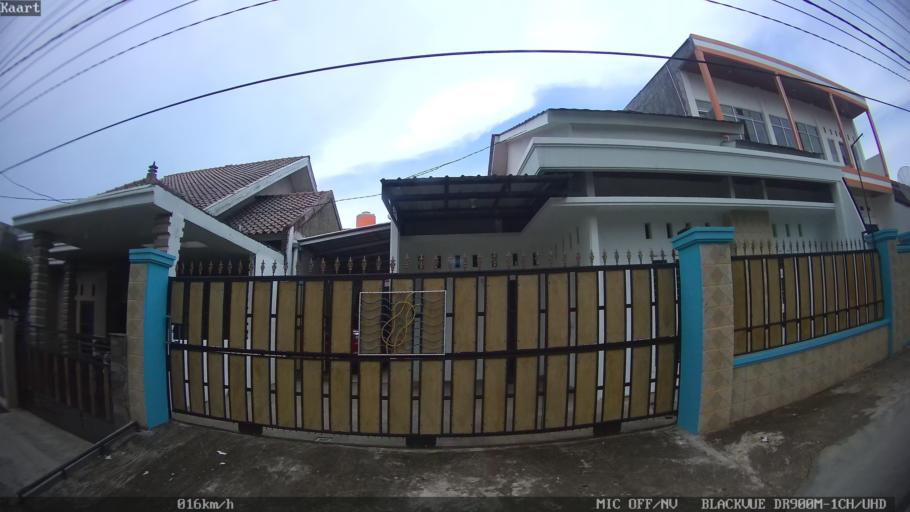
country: ID
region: Lampung
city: Kedaton
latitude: -5.3746
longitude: 105.2131
